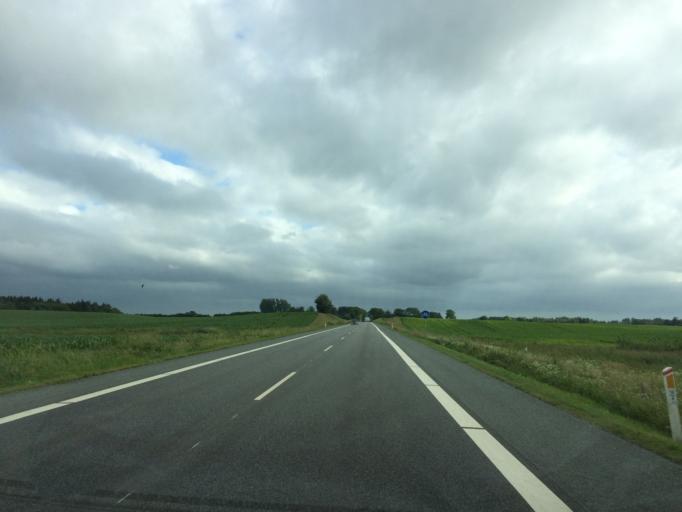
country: DK
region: South Denmark
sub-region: Aabenraa Kommune
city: Krusa
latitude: 54.9206
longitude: 9.4453
